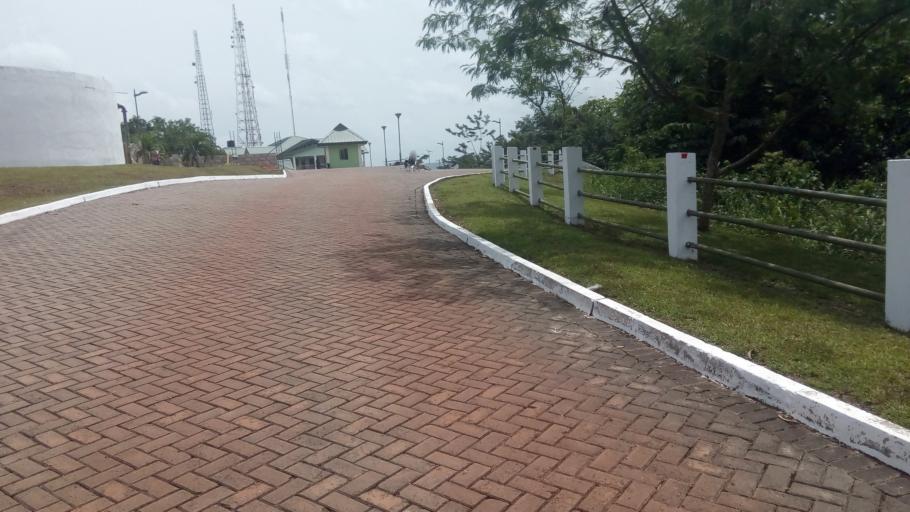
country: GH
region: Western
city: Tarkwa
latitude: 5.2997
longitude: -2.0118
